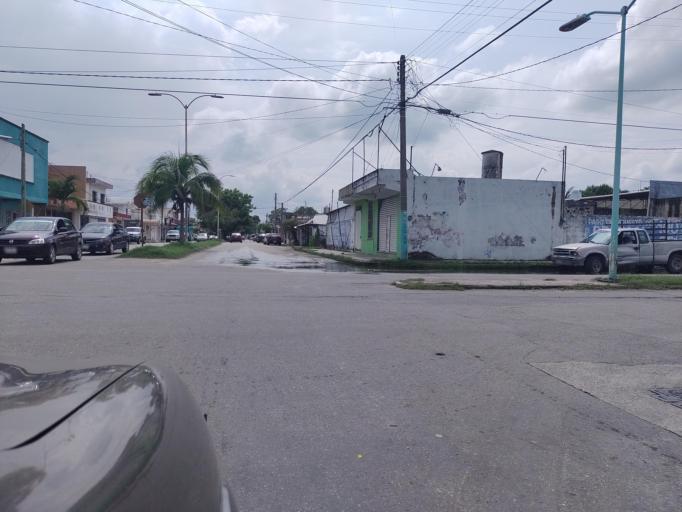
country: MX
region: Quintana Roo
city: Chetumal
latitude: 18.5165
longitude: -88.3085
